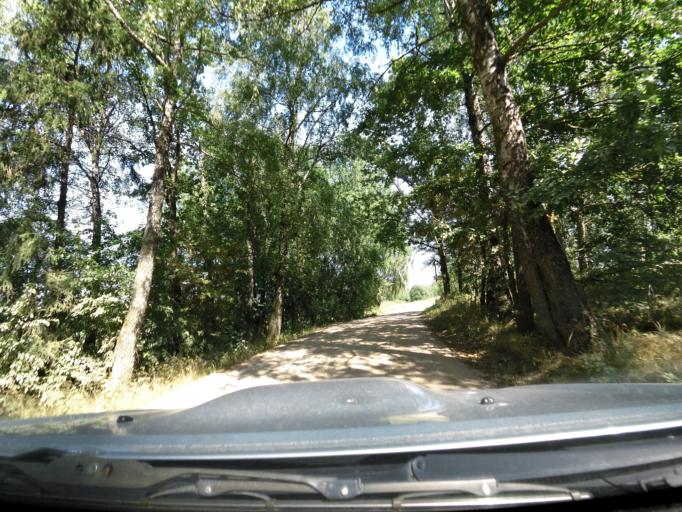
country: LT
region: Vilnius County
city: Pasilaiciai
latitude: 54.8367
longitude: 25.1724
